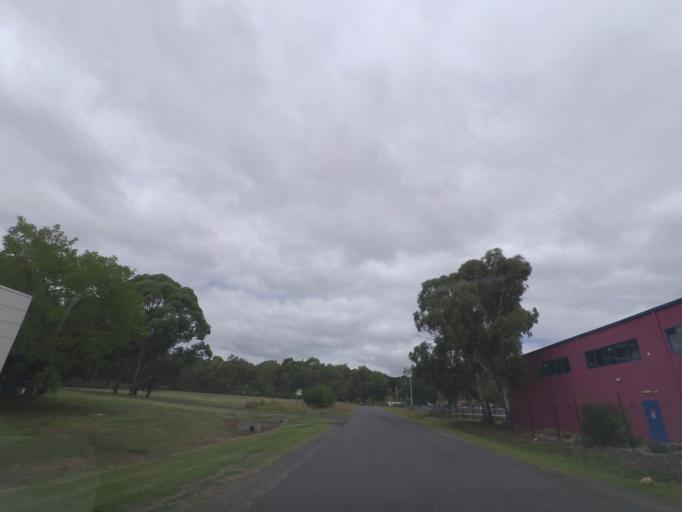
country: AU
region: Victoria
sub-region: Yarra Ranges
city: Lilydale
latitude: -37.7619
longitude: 145.3464
